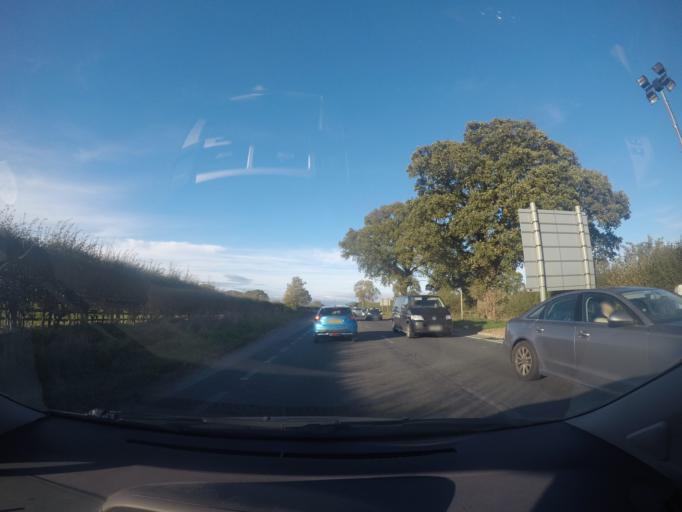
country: GB
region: England
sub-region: City of York
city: Nether Poppleton
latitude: 53.9595
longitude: -1.1504
